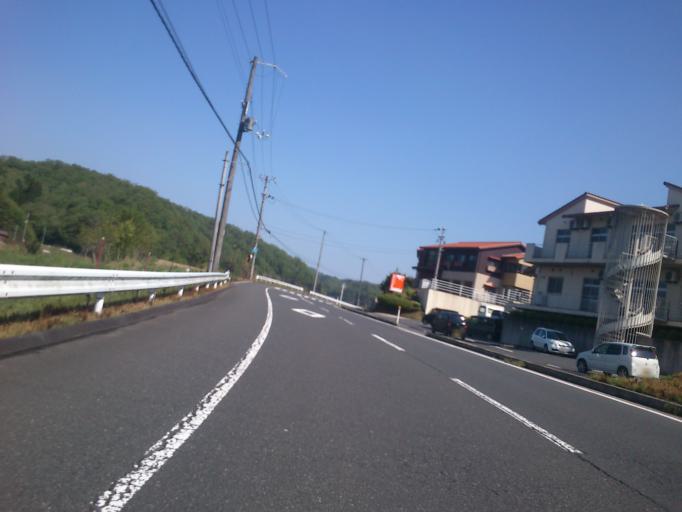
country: JP
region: Kyoto
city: Miyazu
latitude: 35.6011
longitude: 135.1391
